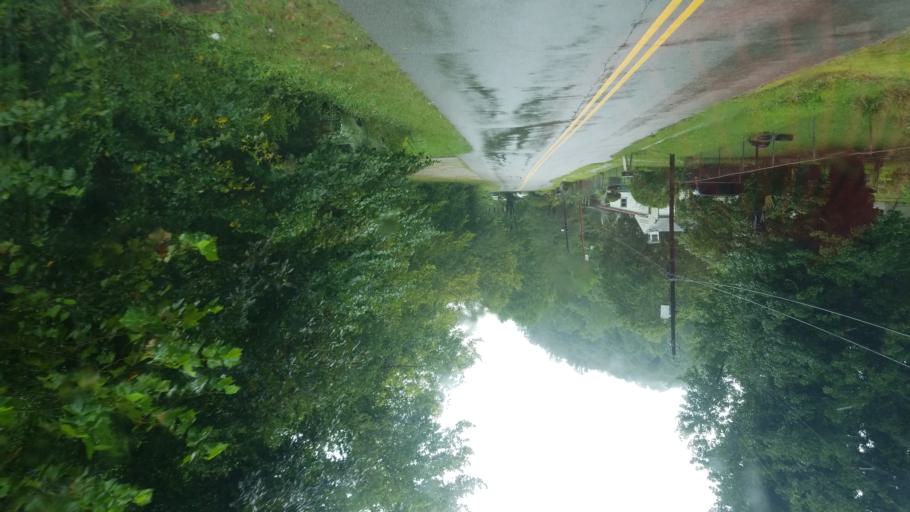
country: US
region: Ohio
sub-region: Scioto County
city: West Portsmouth
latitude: 38.7527
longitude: -83.1006
